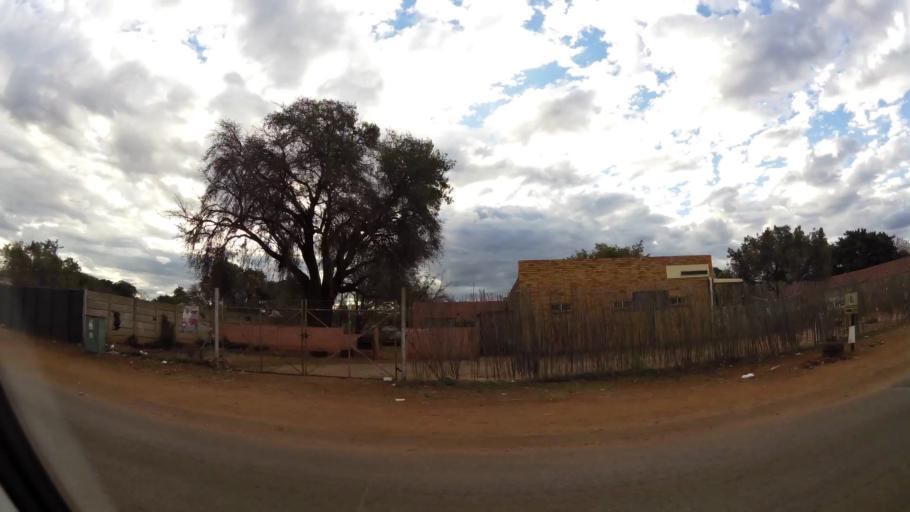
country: ZA
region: Limpopo
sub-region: Waterberg District Municipality
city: Modimolle
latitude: -24.5182
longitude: 28.7191
